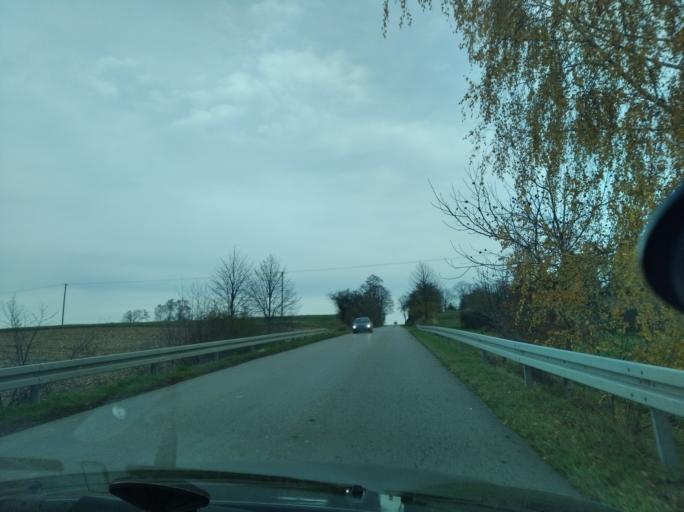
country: PL
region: Subcarpathian Voivodeship
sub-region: Powiat przeworski
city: Nowosielce
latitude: 50.0316
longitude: 22.3967
